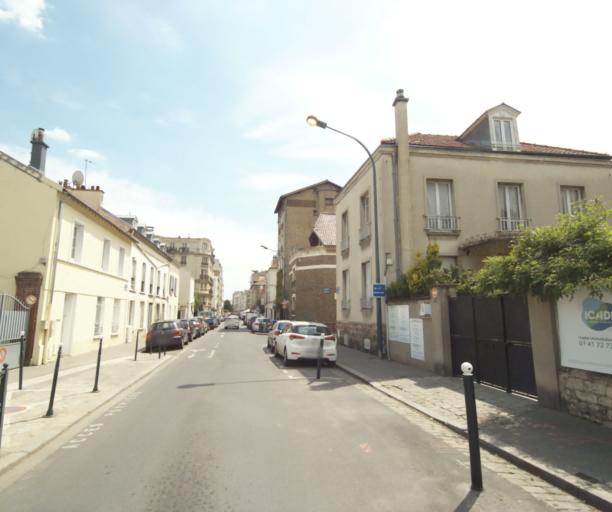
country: FR
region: Ile-de-France
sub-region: Departement des Hauts-de-Seine
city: Asnieres-sur-Seine
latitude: 48.9163
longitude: 2.2849
